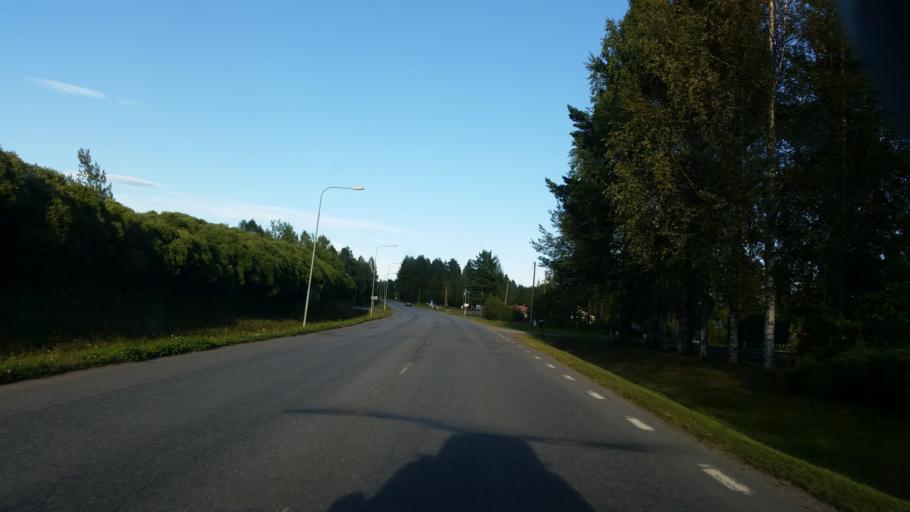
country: SE
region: Vaesterbotten
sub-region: Dorotea Kommun
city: Dorotea
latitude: 64.1071
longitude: 16.1732
